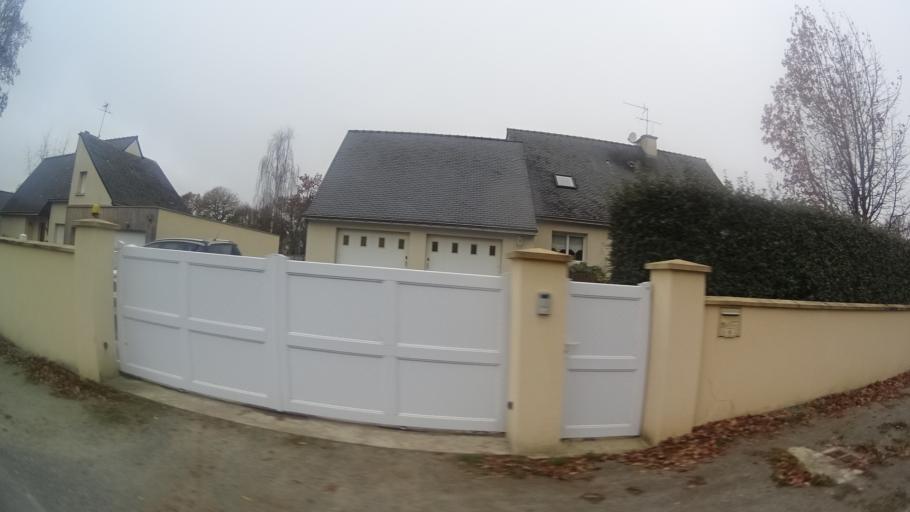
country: FR
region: Brittany
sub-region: Departement d'Ille-et-Vilaine
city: Bains-sur-Oust
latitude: 47.6900
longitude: -2.0789
